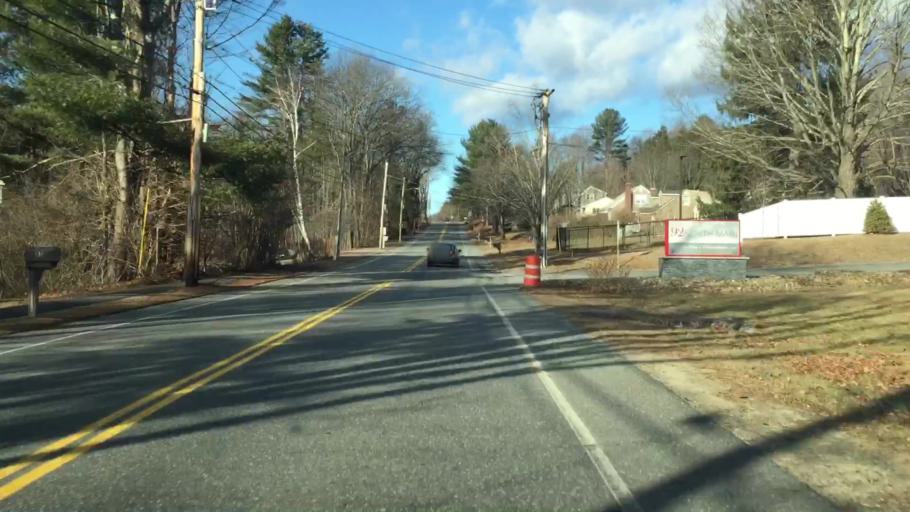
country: US
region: Massachusetts
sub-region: Worcester County
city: West Boylston
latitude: 42.3944
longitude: -71.7937
